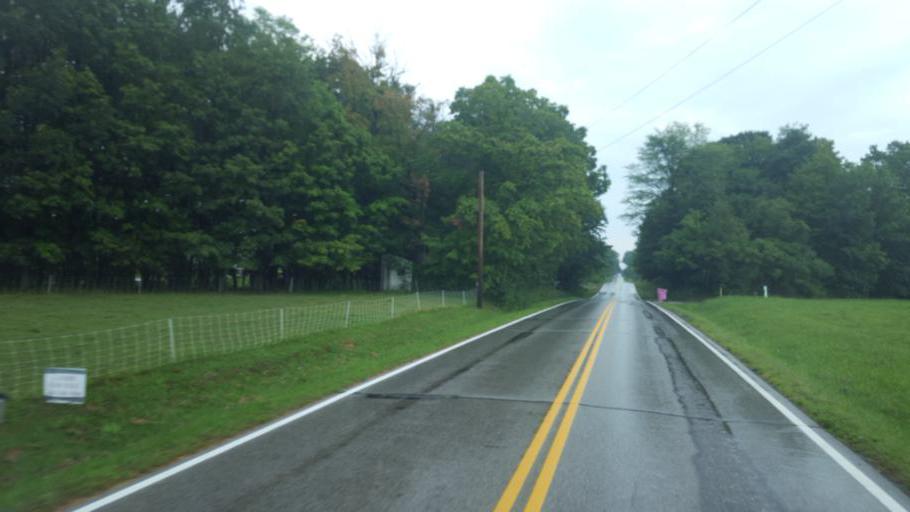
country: US
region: Ohio
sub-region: Geauga County
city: Middlefield
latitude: 41.4035
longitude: -81.0323
